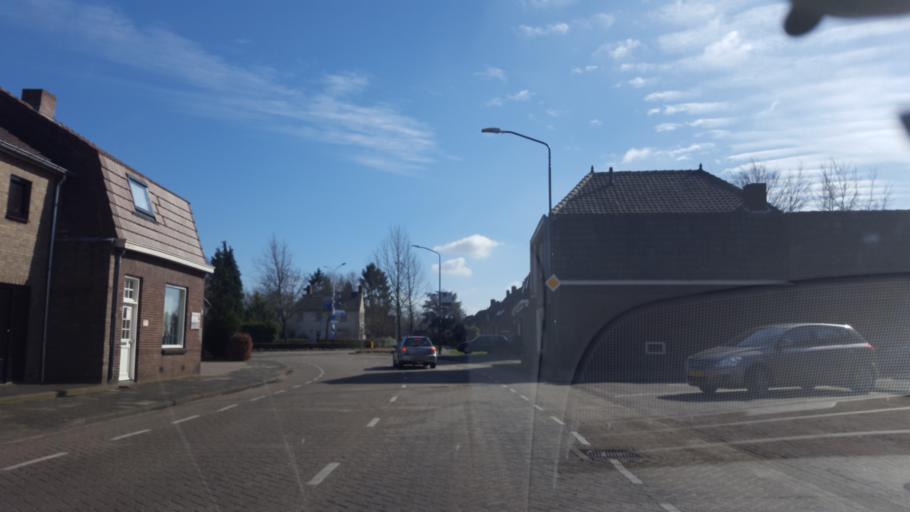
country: NL
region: North Brabant
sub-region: Gemeente Heeze-Leende
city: Heeze
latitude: 51.3730
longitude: 5.5841
